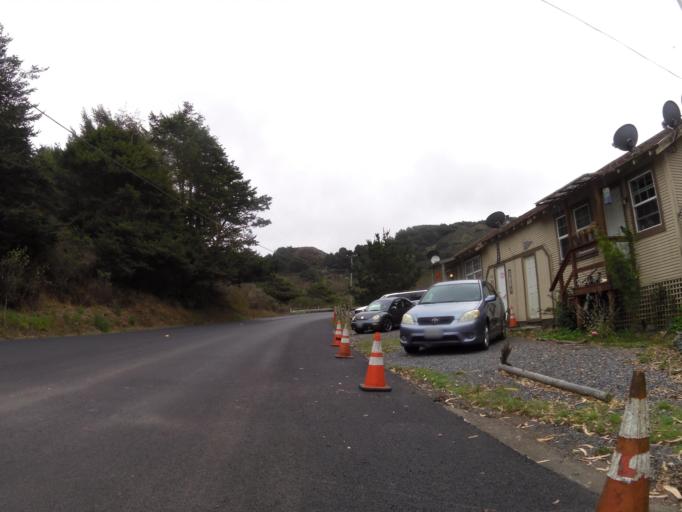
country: US
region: California
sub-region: Sonoma County
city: Monte Rio
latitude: 38.4332
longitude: -123.1006
